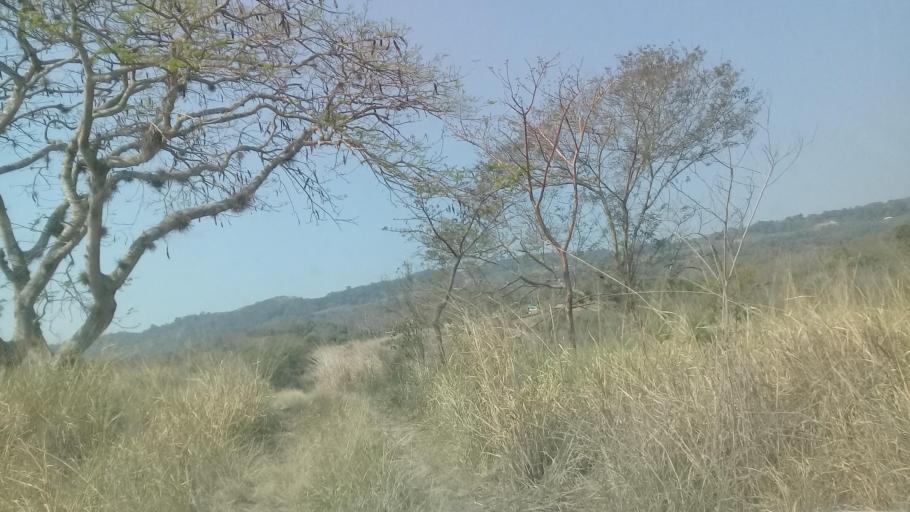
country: MX
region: Veracruz
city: El Castillo
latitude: 19.5767
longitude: -96.8327
